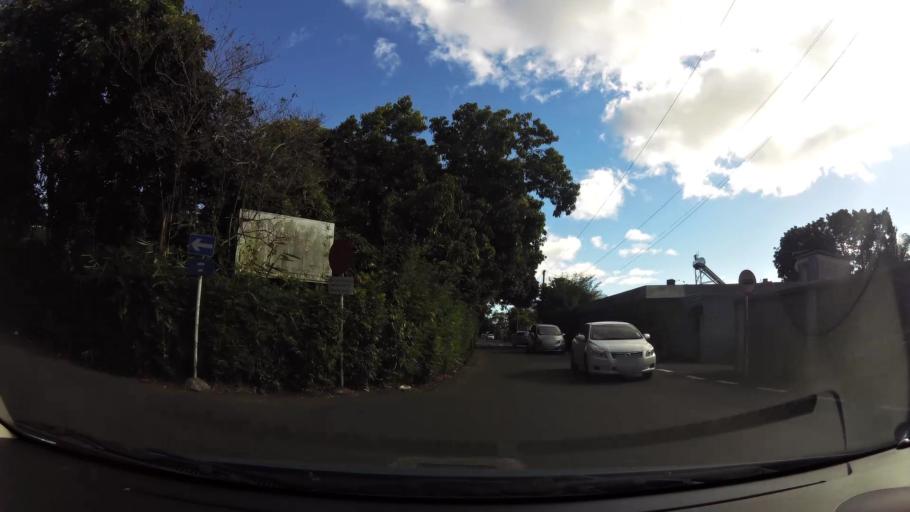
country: MU
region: Plaines Wilhems
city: Vacoas
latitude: -20.2948
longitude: 57.4917
